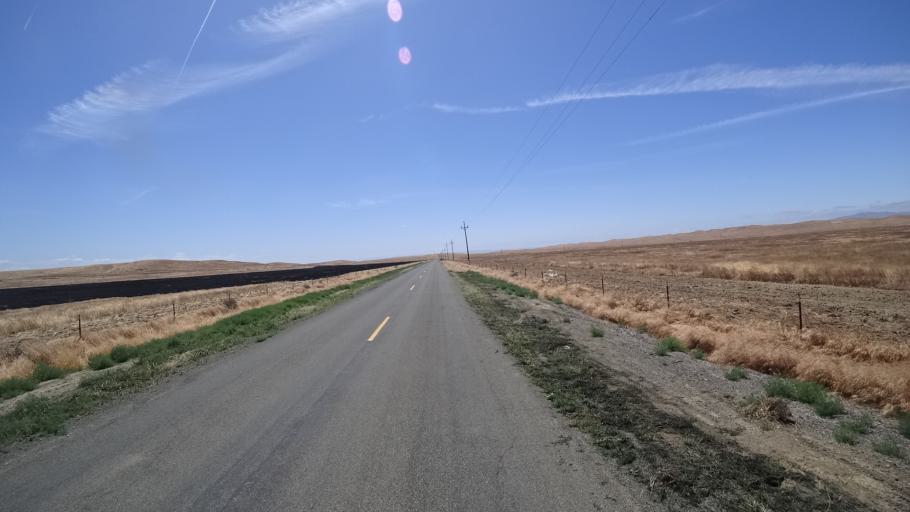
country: US
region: California
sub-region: Kings County
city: Kettleman City
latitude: 35.8429
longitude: -119.9153
